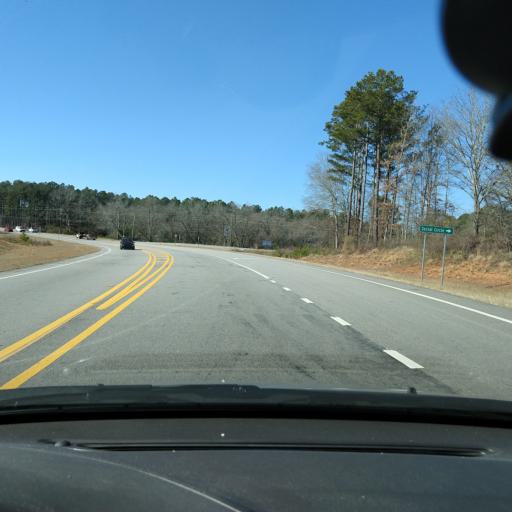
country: US
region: Georgia
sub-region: Walton County
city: Social Circle
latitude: 33.6408
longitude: -83.7216
